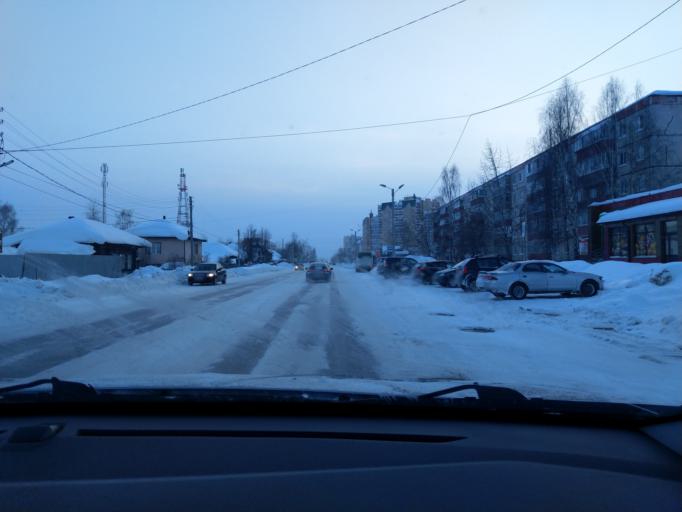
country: RU
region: Perm
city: Dobryanka
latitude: 58.4698
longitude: 56.4056
